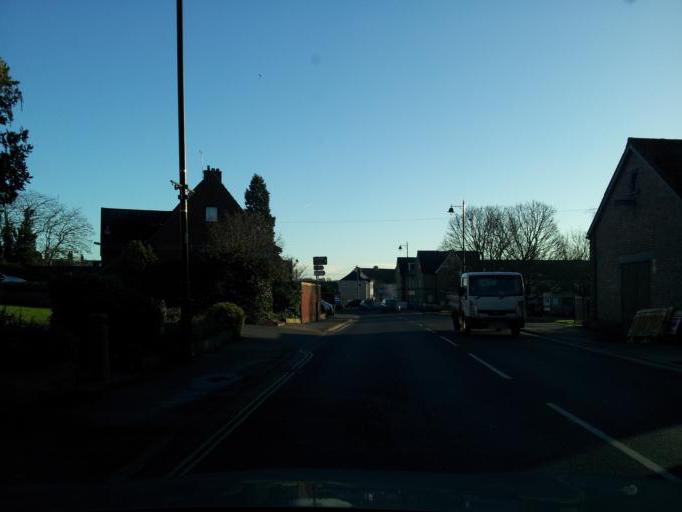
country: GB
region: England
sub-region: Suffolk
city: Woodbridge
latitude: 52.0908
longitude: 1.3154
